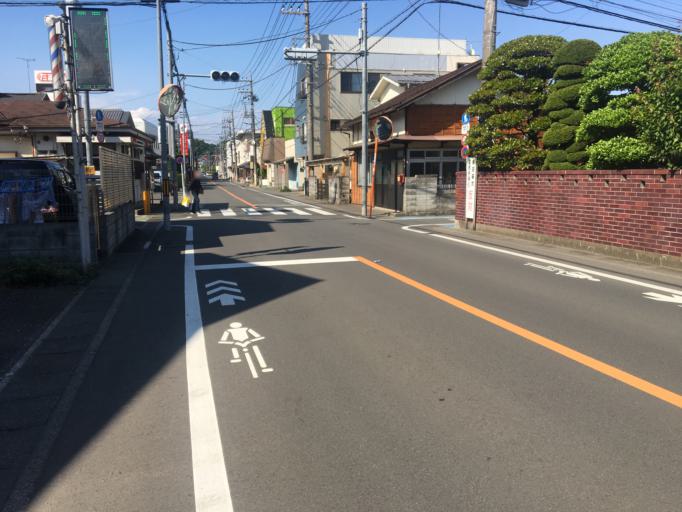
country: JP
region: Tokyo
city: Fussa
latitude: 35.7708
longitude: 139.3499
